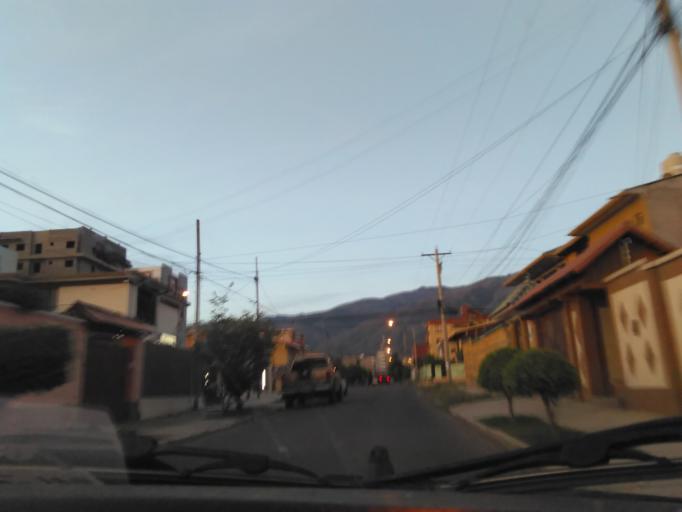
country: BO
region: Cochabamba
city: Cochabamba
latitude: -17.3764
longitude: -66.1657
